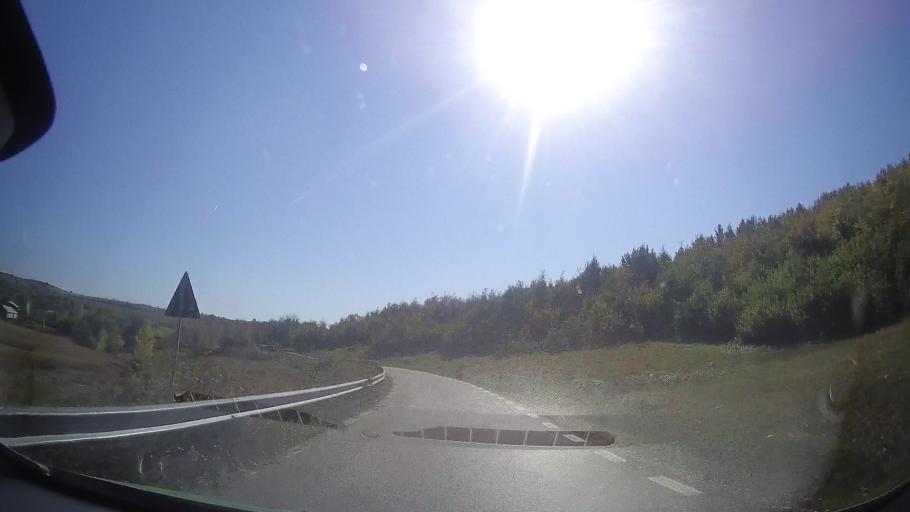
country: RO
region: Timis
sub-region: Comuna Ohaba Lunga
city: Ohaba Lunga
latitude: 45.9076
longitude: 21.9760
